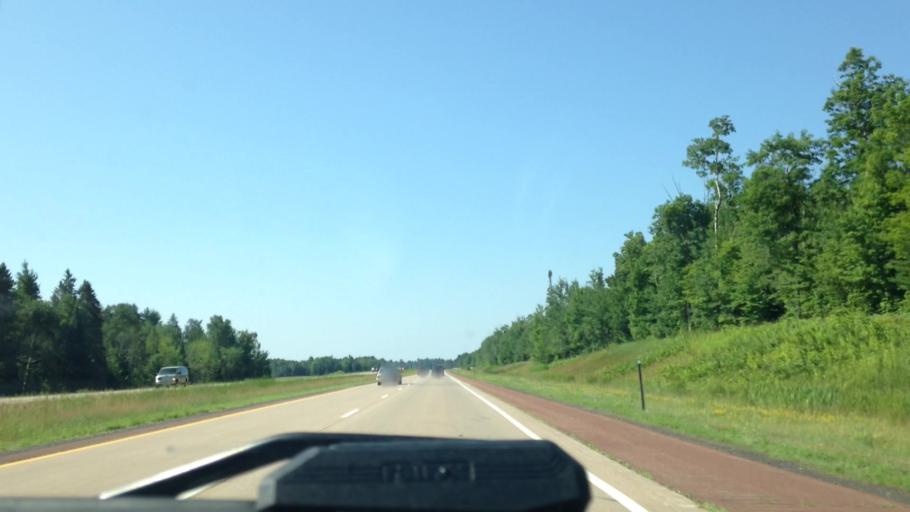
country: US
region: Wisconsin
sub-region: Douglas County
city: Lake Nebagamon
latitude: 46.3710
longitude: -91.8277
